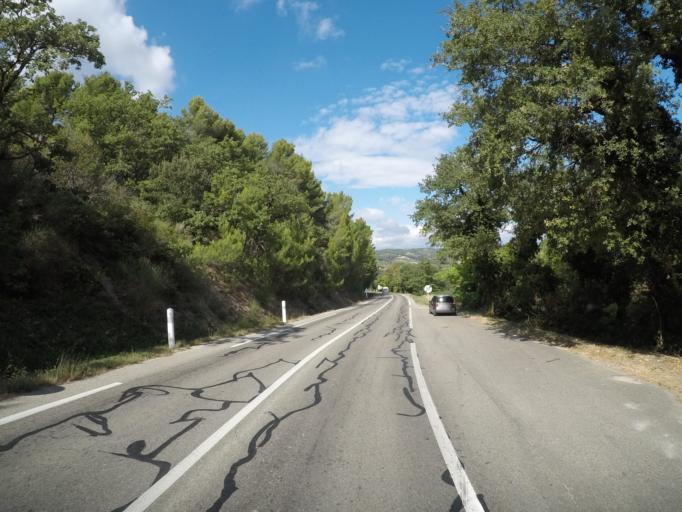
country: FR
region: Provence-Alpes-Cote d'Azur
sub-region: Departement du Vaucluse
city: Visan
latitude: 44.2783
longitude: 4.9945
